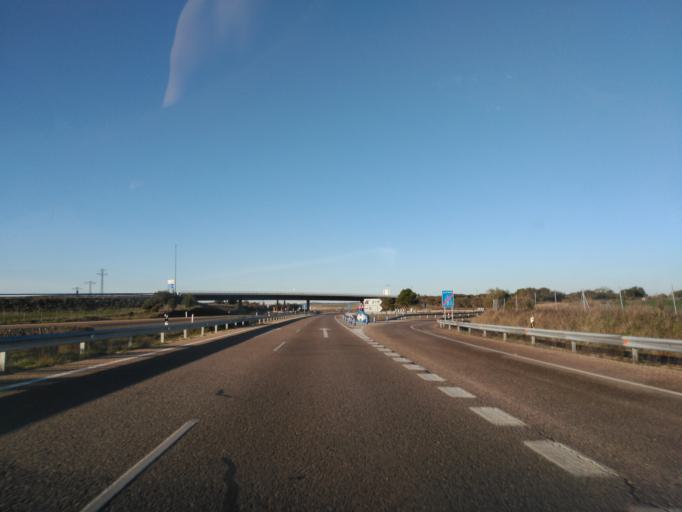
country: ES
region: Castille and Leon
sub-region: Provincia de Salamanca
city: Pajares de la Laguna
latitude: 41.0908
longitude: -5.5031
